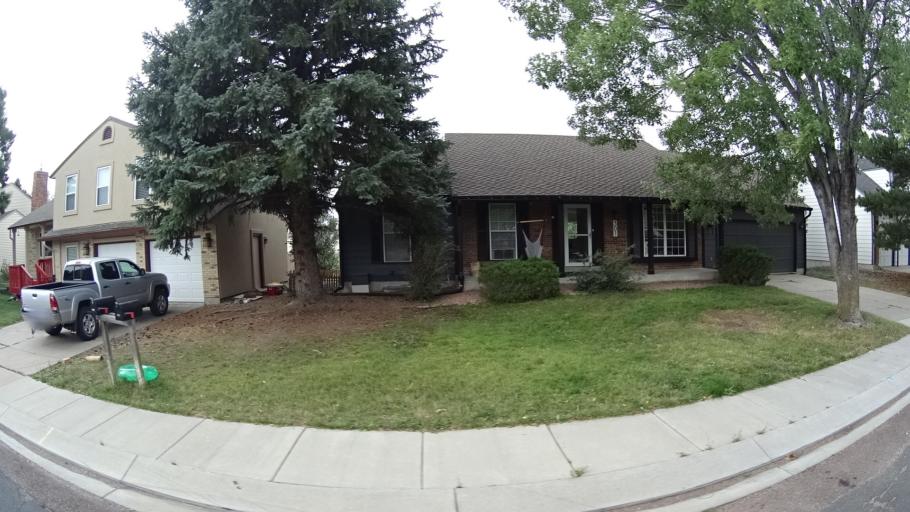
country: US
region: Colorado
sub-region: El Paso County
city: Air Force Academy
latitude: 38.9223
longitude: -104.8338
